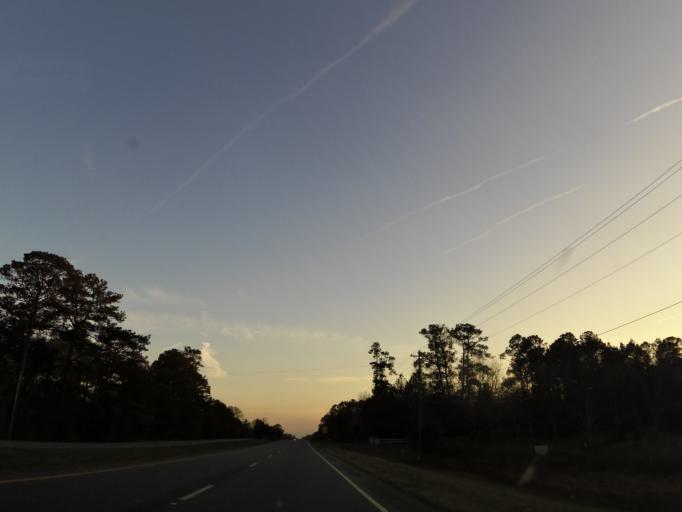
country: US
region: Georgia
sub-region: Lee County
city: Leesburg
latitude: 31.7063
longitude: -84.1727
